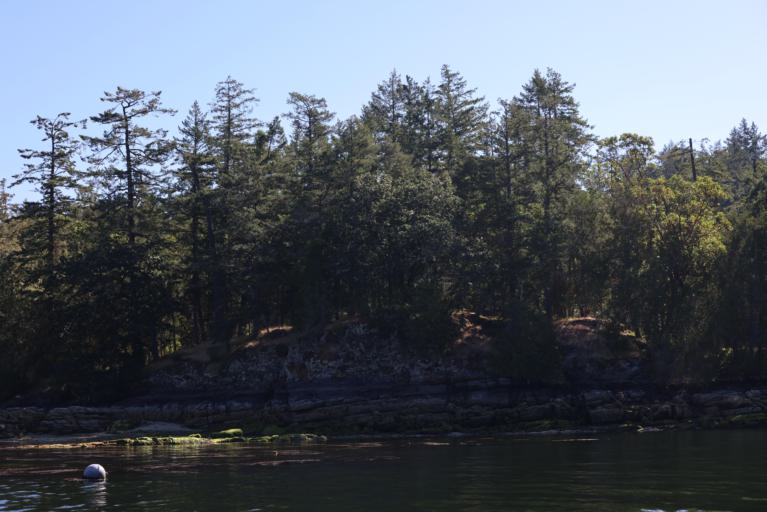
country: CA
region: British Columbia
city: North Cowichan
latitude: 48.8004
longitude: -123.5983
